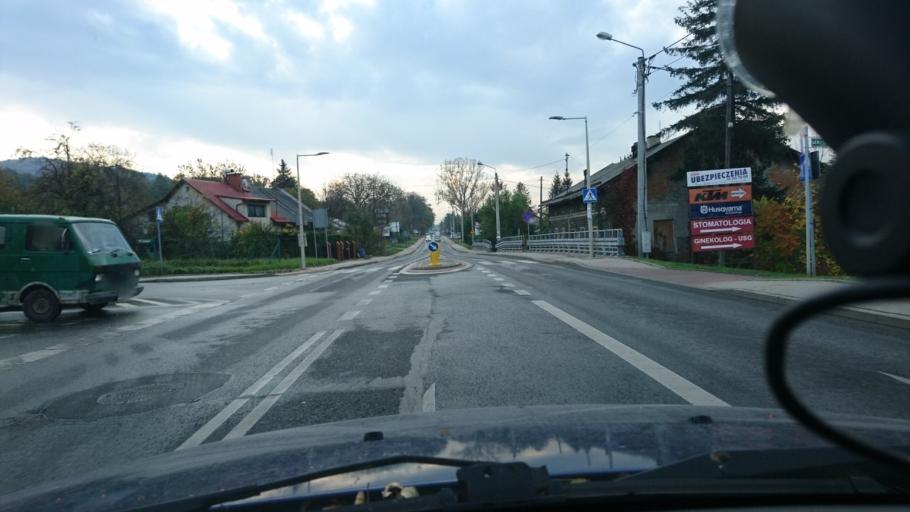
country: PL
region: Silesian Voivodeship
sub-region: Bielsko-Biala
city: Bielsko-Biala
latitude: 49.7966
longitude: 19.0640
